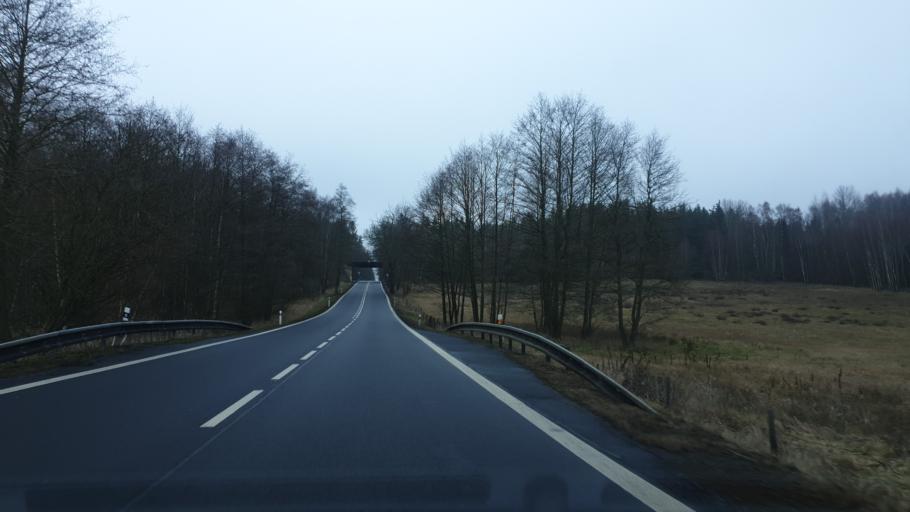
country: CZ
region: Karlovarsky
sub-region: Okres Cheb
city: Frantiskovy Lazne
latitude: 50.1436
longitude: 12.3327
